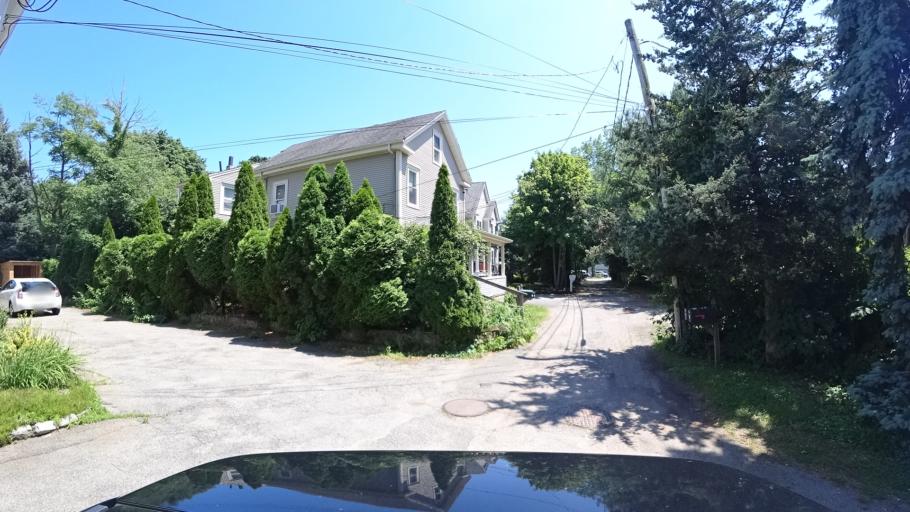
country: US
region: Massachusetts
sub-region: Norfolk County
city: Dedham
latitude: 42.2439
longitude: -71.1453
